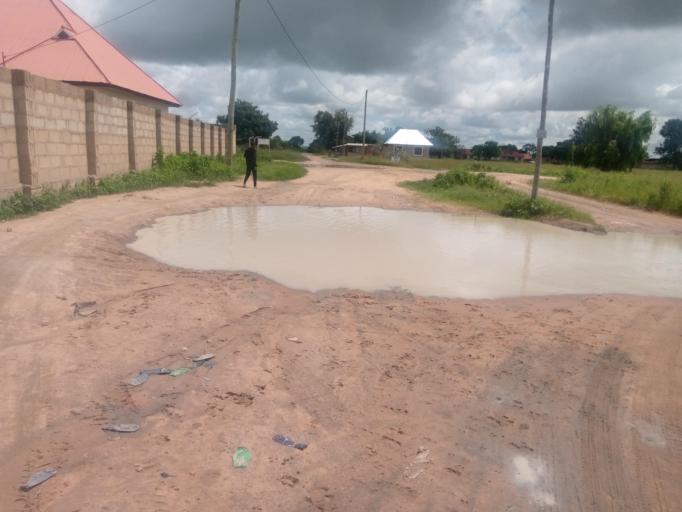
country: TZ
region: Dodoma
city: Dodoma
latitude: -6.1212
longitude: 35.7396
